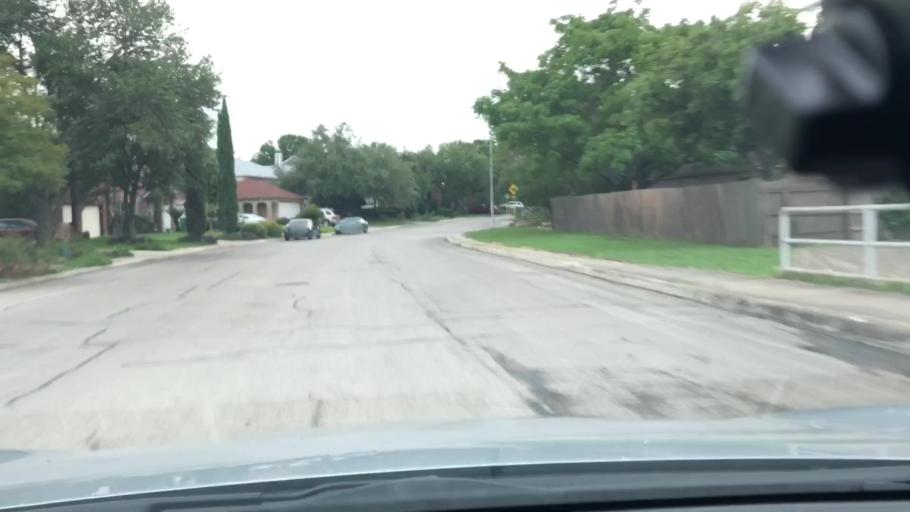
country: US
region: Texas
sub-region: Bexar County
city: Leon Valley
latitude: 29.4994
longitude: -98.6647
